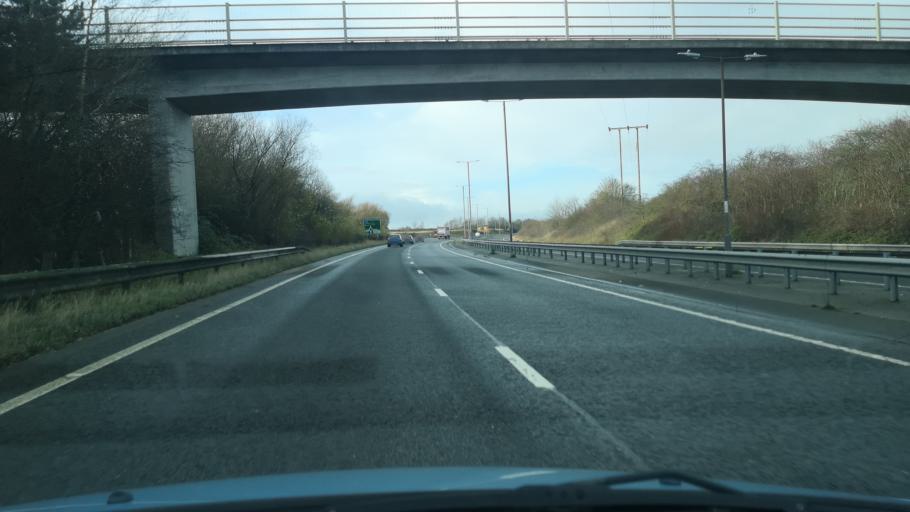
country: GB
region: England
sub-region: Barnsley
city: Hoyland Nether
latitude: 53.5100
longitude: -1.4240
